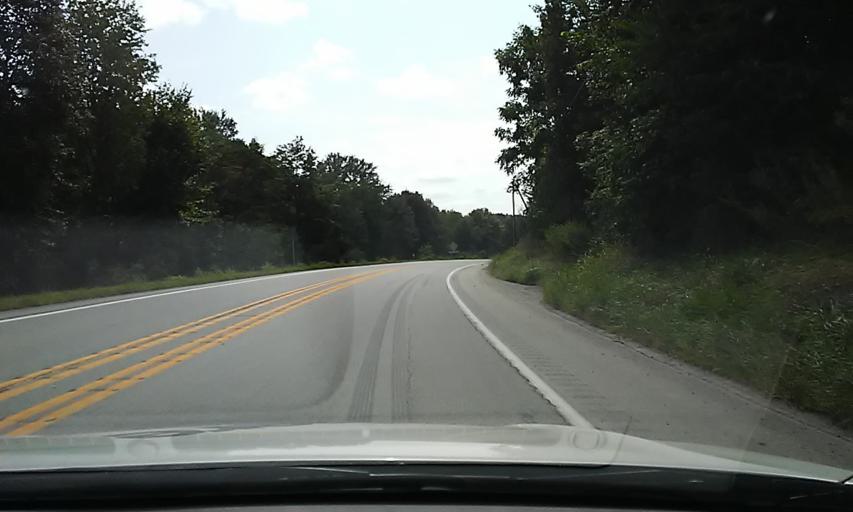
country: US
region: Pennsylvania
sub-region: Indiana County
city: Clymer
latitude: 40.7664
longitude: -79.0571
